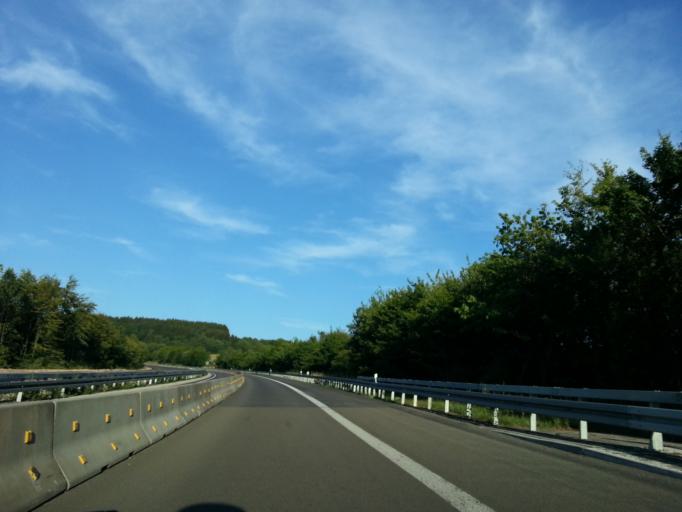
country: DE
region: Rheinland-Pfalz
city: Neuhutten
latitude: 49.5892
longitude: 7.0111
